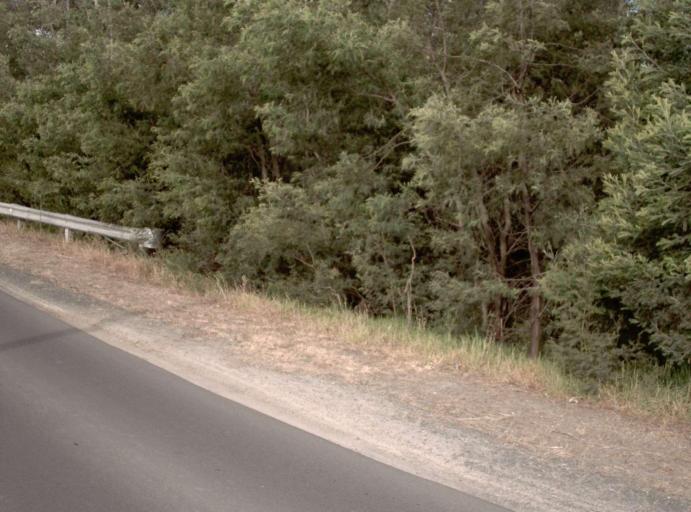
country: AU
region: Victoria
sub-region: Wellington
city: Heyfield
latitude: -37.9860
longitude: 146.7801
